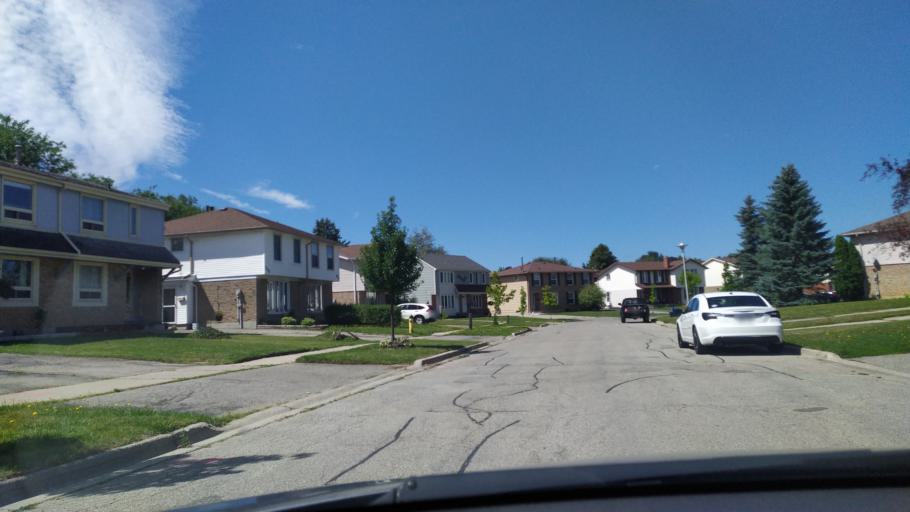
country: CA
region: Ontario
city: Stratford
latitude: 43.3724
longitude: -80.9450
